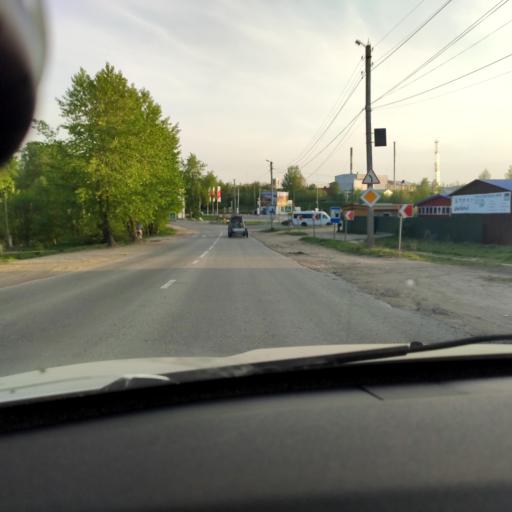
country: RU
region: Perm
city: Polazna
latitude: 58.2877
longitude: 56.4110
